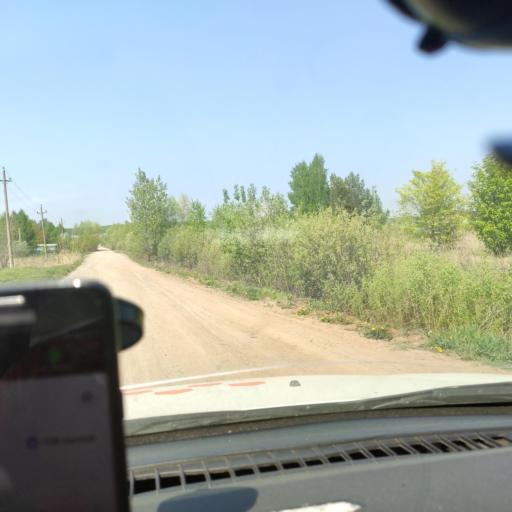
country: RU
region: Bashkortostan
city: Ulukulevo
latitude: 54.5724
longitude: 56.3022
